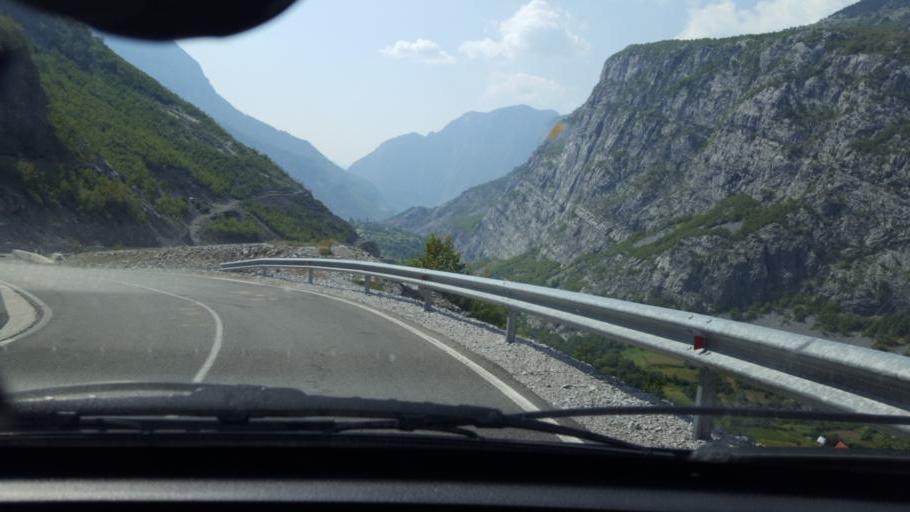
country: AL
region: Shkoder
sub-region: Rrethi i Malesia e Madhe
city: Kastrat
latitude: 42.5242
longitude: 19.6328
